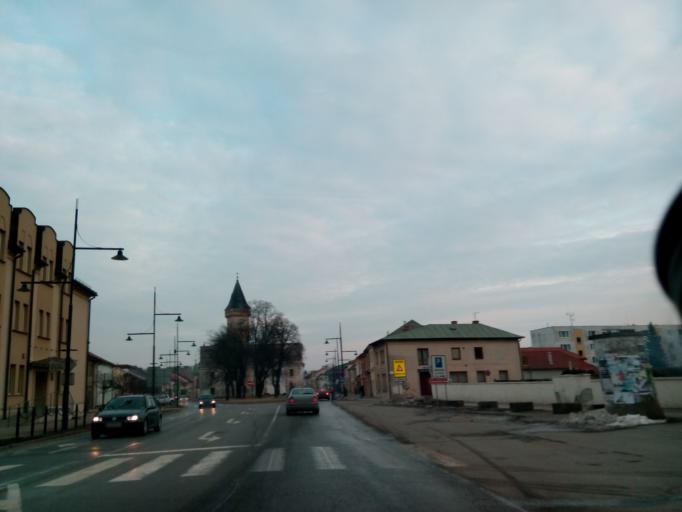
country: SK
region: Presovsky
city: Sabinov
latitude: 49.1037
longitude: 21.0934
